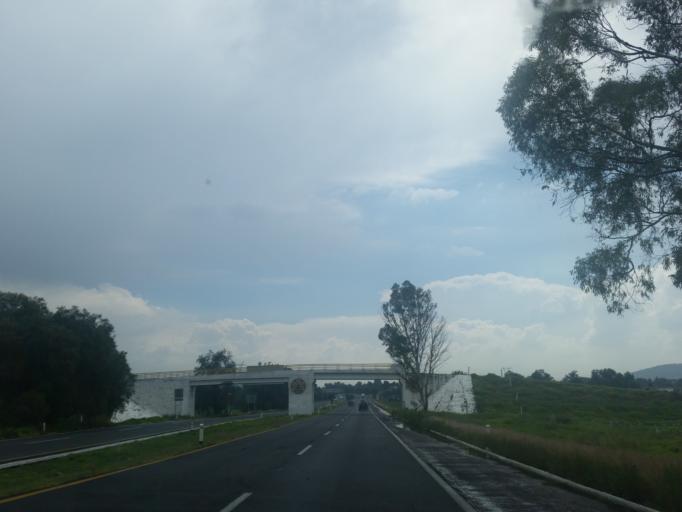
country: MX
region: Mexico
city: Acolman
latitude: 19.6287
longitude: -98.9197
